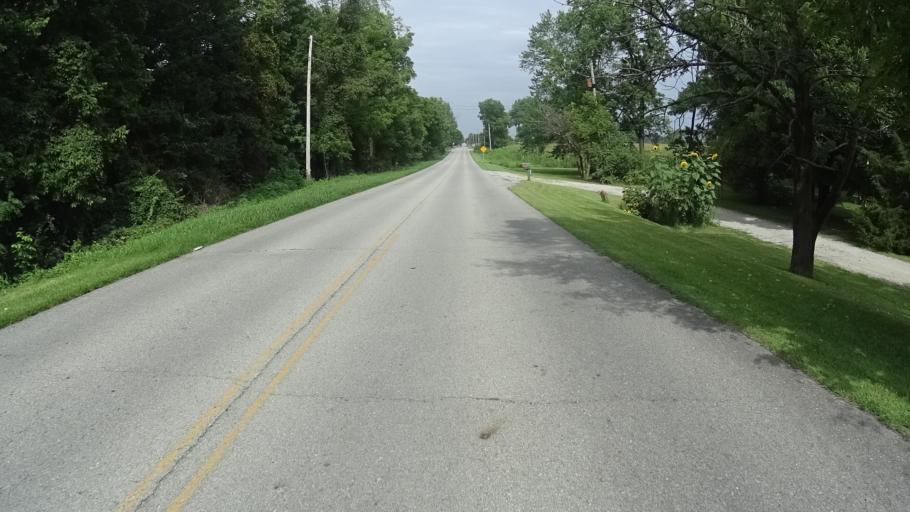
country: US
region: Indiana
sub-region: Madison County
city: Pendleton
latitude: 40.0186
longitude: -85.7674
